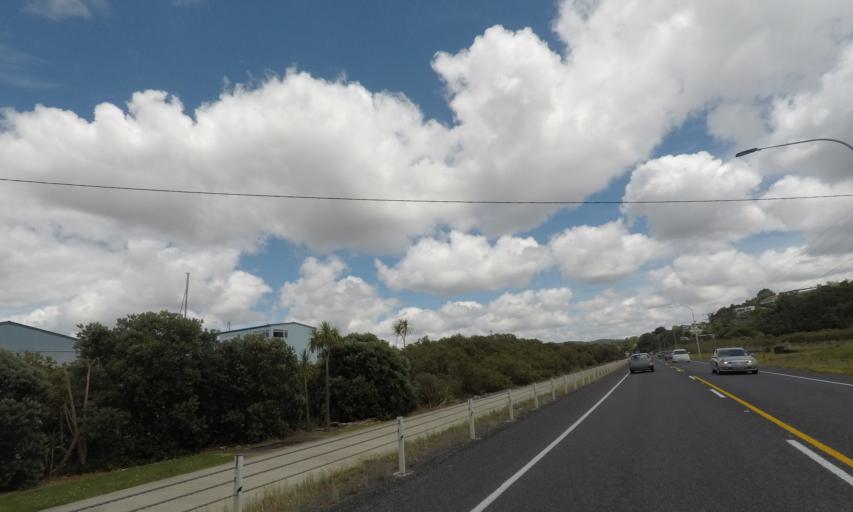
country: NZ
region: Northland
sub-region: Whangarei
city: Whangarei
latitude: -35.7336
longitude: 174.3480
